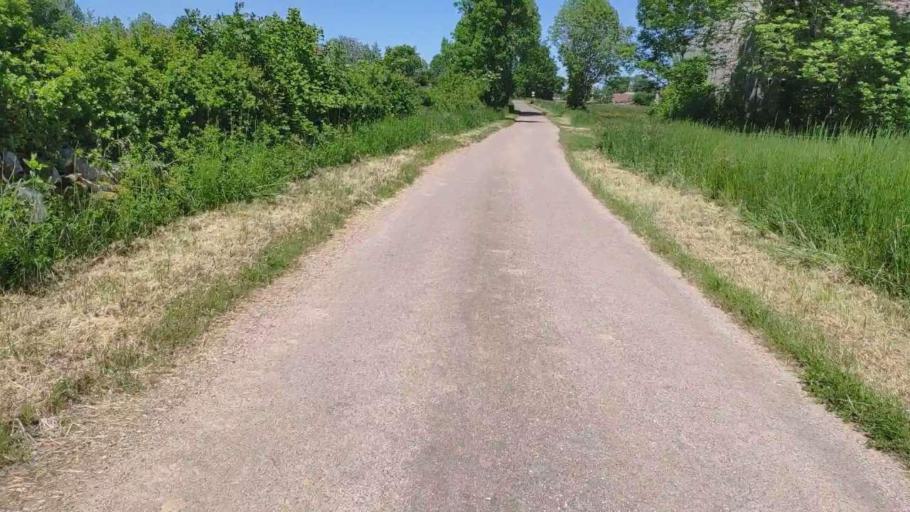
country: FR
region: Franche-Comte
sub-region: Departement du Jura
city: Perrigny
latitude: 46.7147
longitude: 5.6504
